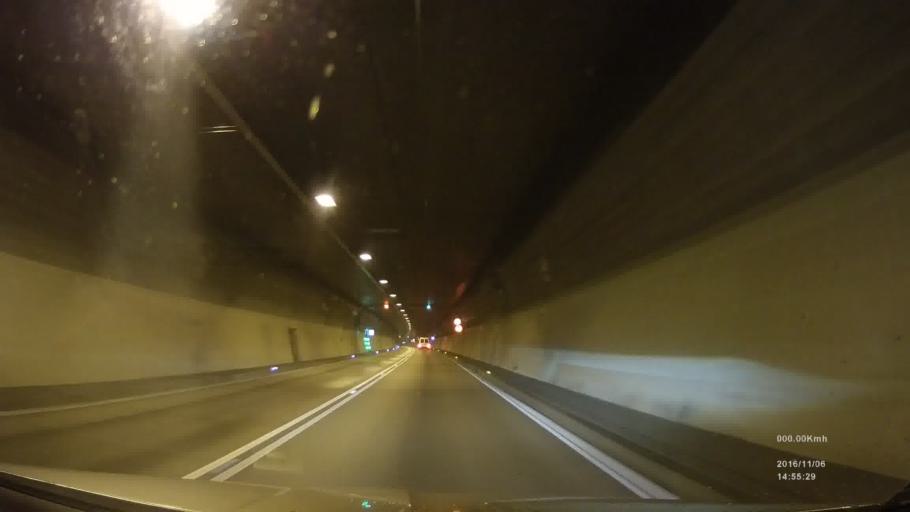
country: SK
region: Kosicky
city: Krompachy
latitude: 48.9995
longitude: 20.8923
